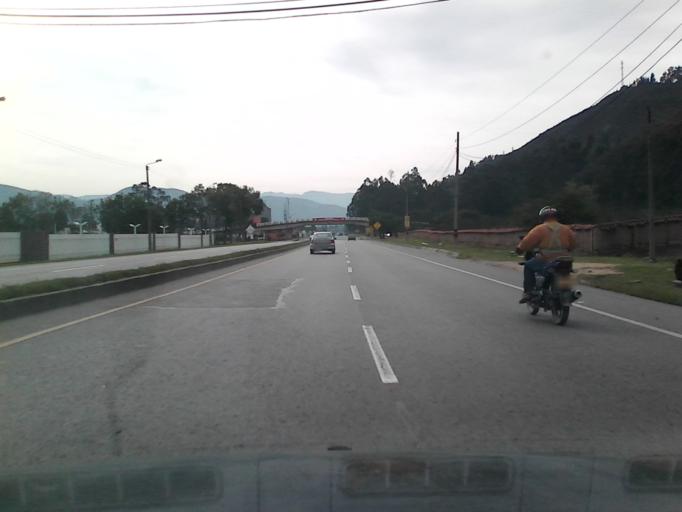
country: CO
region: Boyaca
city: Duitama
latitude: 5.8072
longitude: -73.0093
